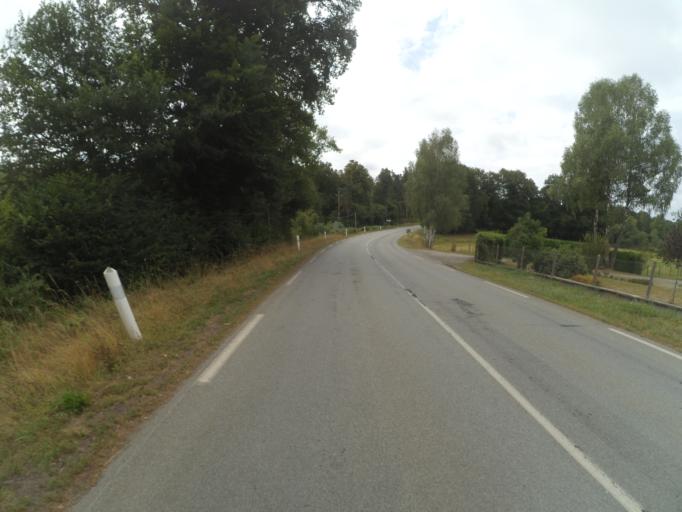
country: FR
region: Limousin
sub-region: Departement de la Correze
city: Ussel
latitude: 45.5977
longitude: 2.2921
